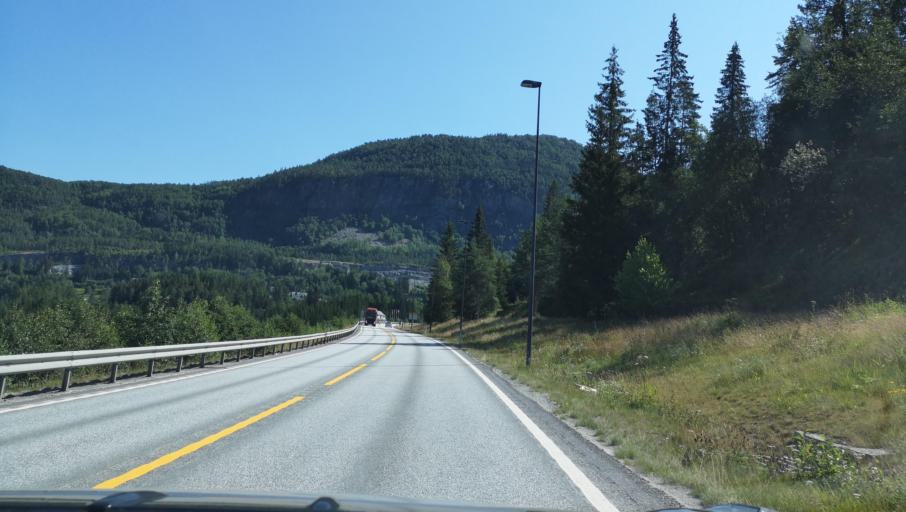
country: NO
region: Hordaland
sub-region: Voss
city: Voss
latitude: 60.6285
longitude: 6.5177
